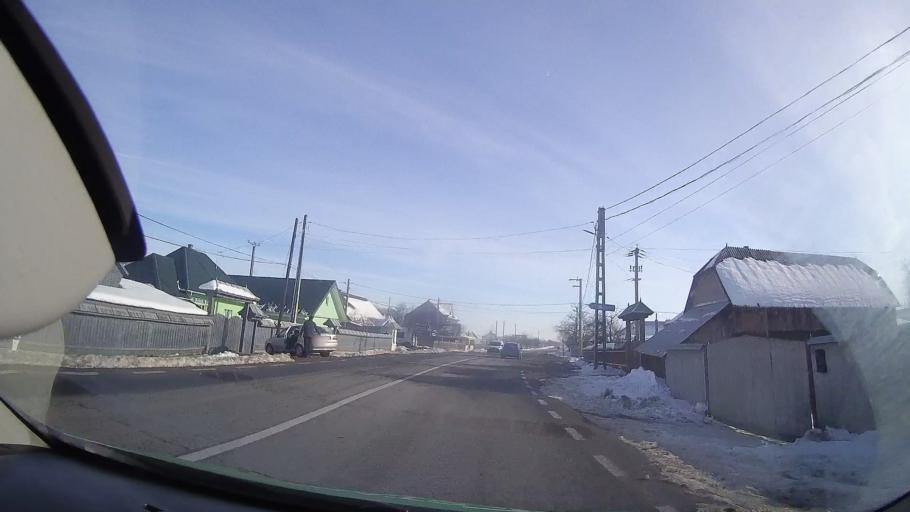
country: RO
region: Neamt
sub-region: Comuna Cracaoani
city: Cracaoani
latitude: 47.0881
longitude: 26.3296
